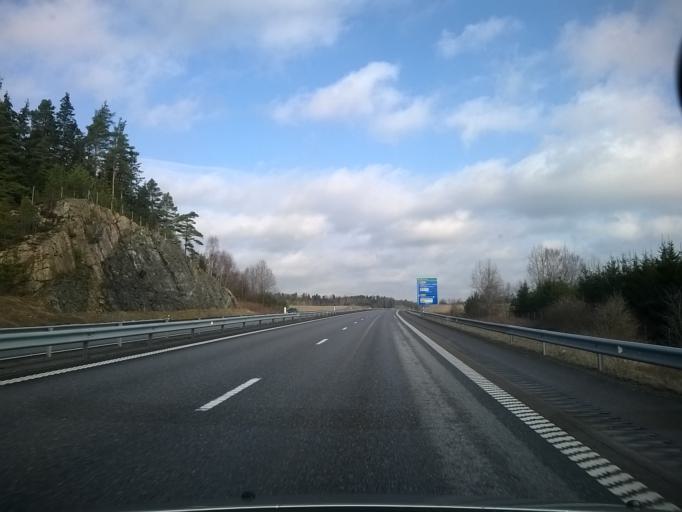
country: SE
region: Vaestra Goetaland
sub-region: Uddevalla Kommun
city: Uddevalla
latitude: 58.3381
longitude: 11.8268
